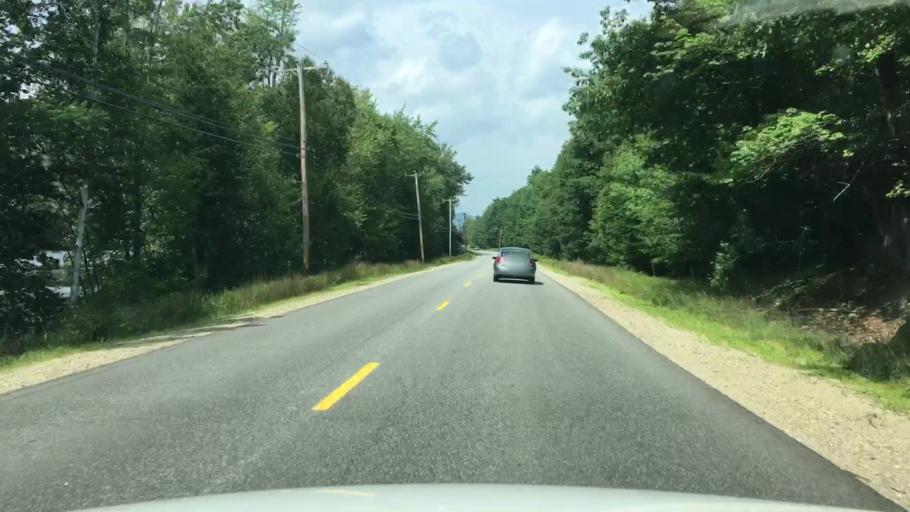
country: US
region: Maine
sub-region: Oxford County
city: Rumford
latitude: 44.5294
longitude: -70.5360
